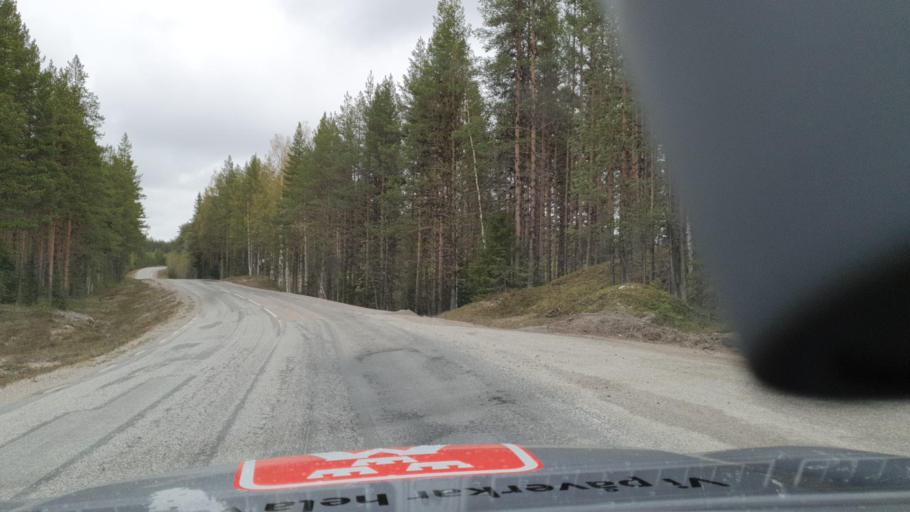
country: SE
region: Vaesterbotten
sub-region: Asele Kommun
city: Asele
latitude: 63.6933
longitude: 17.2268
